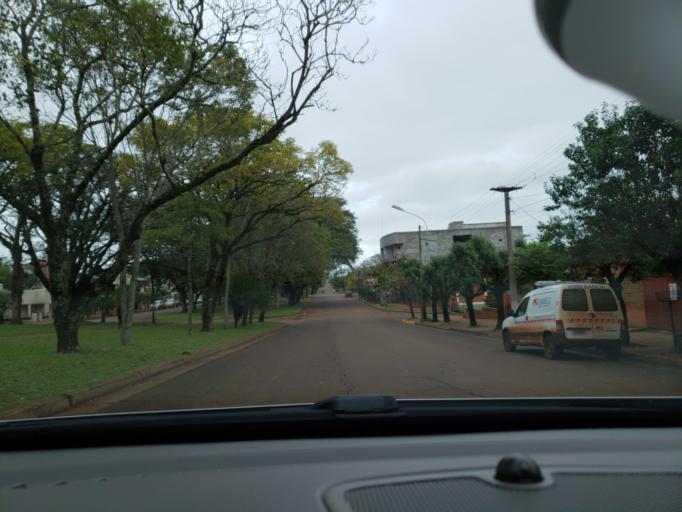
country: AR
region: Misiones
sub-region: Departamento de Apostoles
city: Apostoles
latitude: -27.9167
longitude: -55.7580
